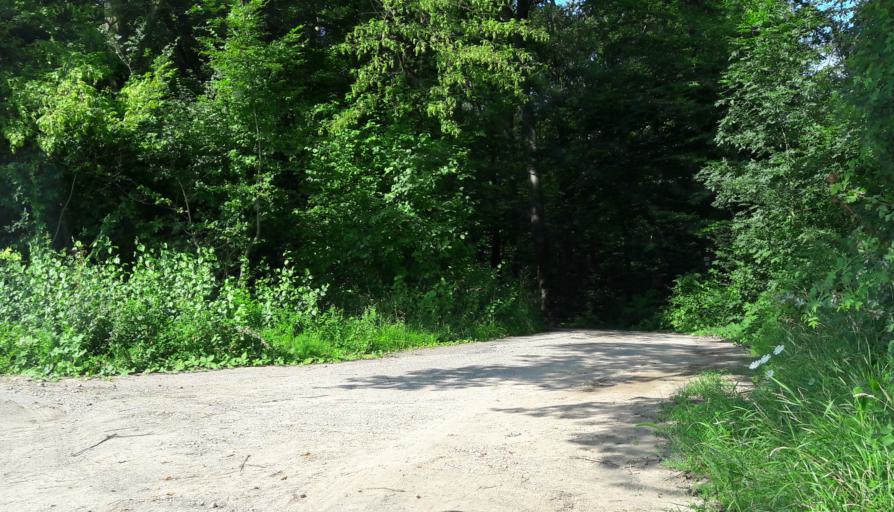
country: DE
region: Baden-Wuerttemberg
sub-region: Regierungsbezirk Stuttgart
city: Erlenbach
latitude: 49.1982
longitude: 9.2585
